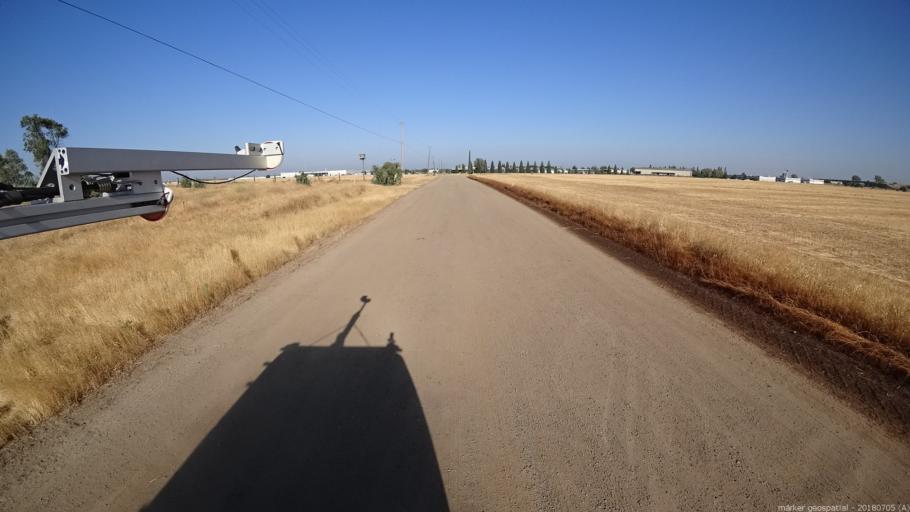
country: US
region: California
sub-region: Madera County
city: Madera Acres
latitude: 36.9900
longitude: -120.0964
